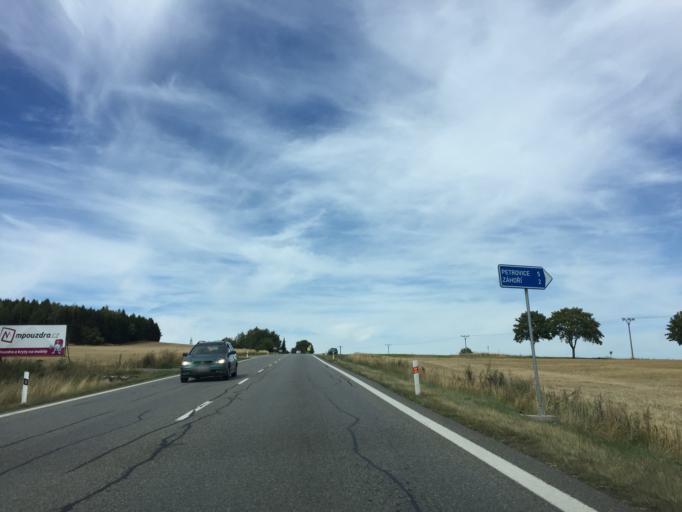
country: CZ
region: Jihocesky
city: Chotoviny
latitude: 49.5510
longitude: 14.6656
